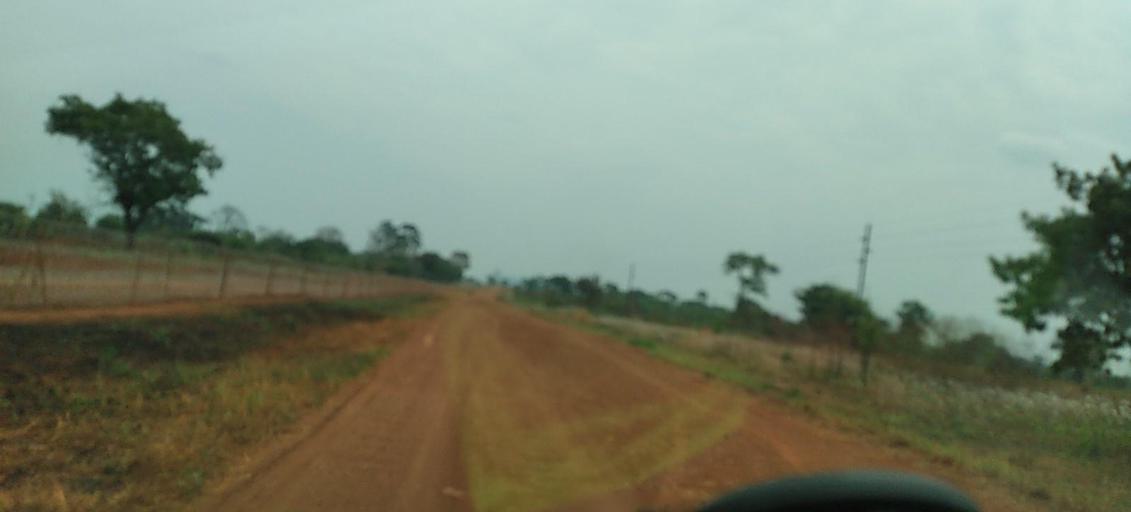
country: ZM
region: North-Western
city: Kansanshi
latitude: -12.0850
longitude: 26.4827
